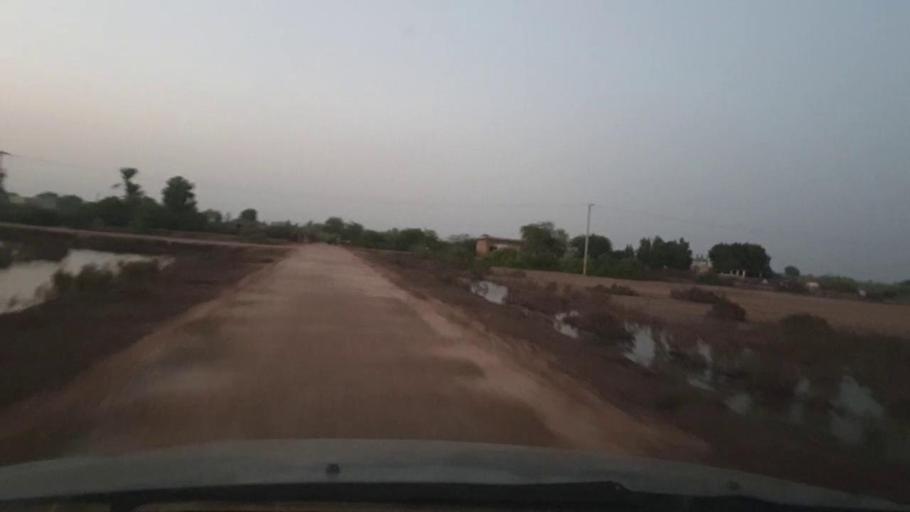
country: PK
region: Sindh
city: Tando Ghulam Ali
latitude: 25.1166
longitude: 68.9795
